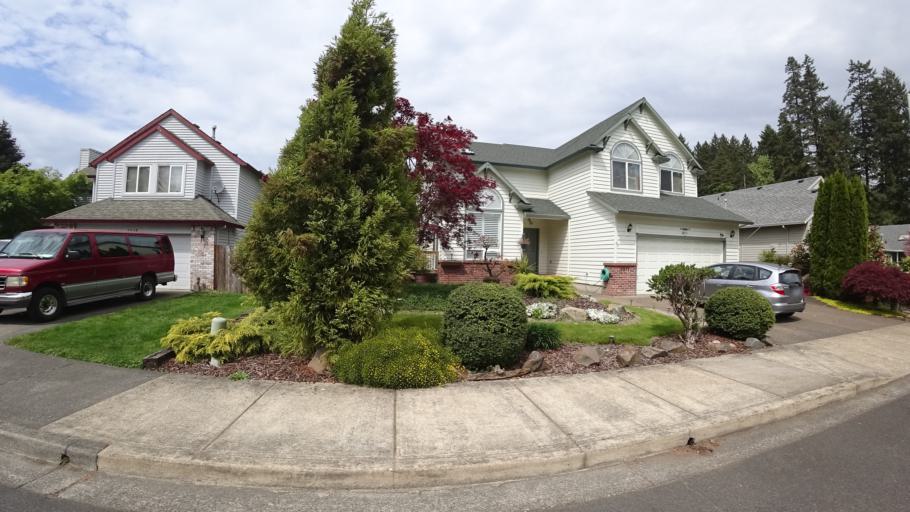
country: US
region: Oregon
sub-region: Washington County
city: Rockcreek
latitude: 45.5183
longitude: -122.9209
